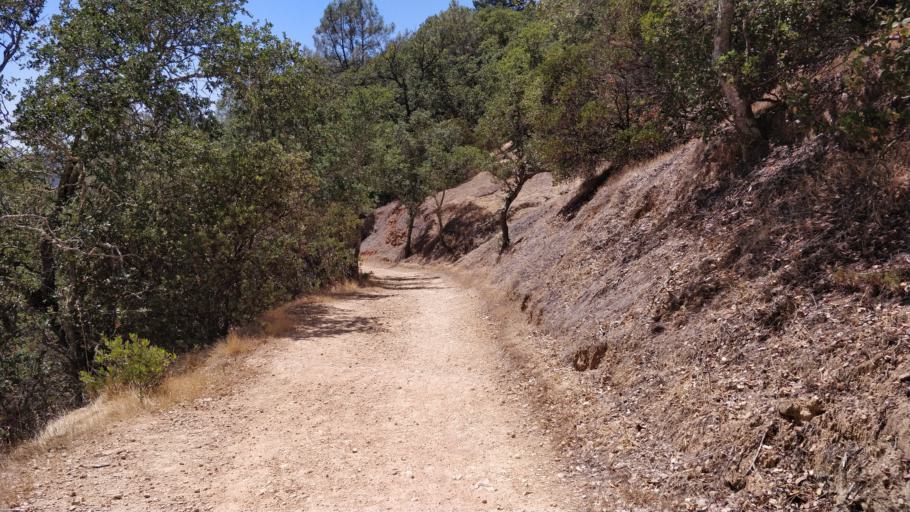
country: US
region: California
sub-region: Napa County
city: Calistoga
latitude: 38.5960
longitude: -122.5703
